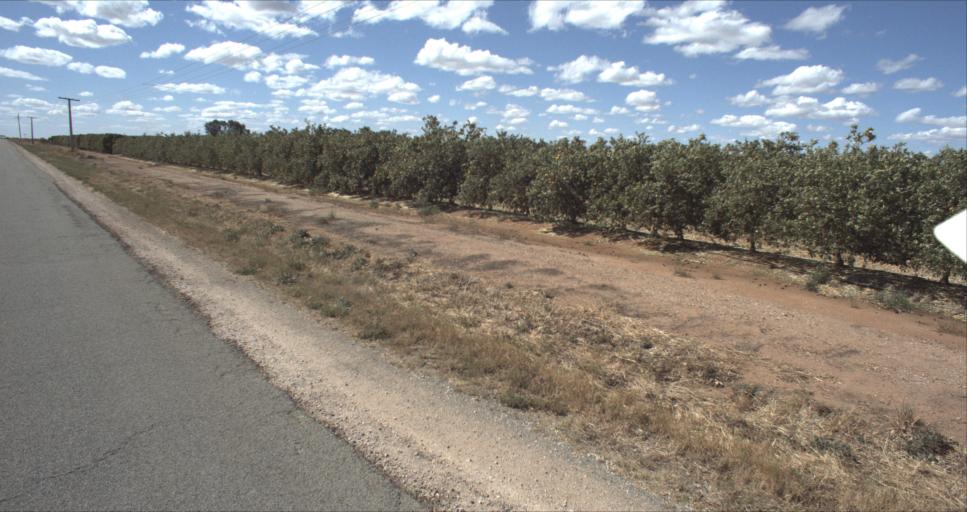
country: AU
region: New South Wales
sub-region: Leeton
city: Leeton
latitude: -34.5077
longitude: 146.2223
